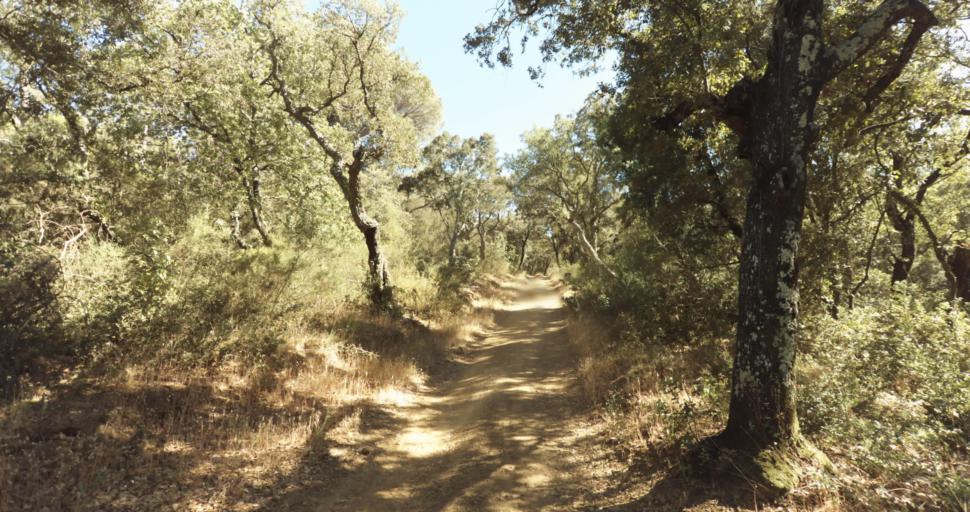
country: FR
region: Provence-Alpes-Cote d'Azur
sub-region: Departement du Var
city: Gassin
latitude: 43.2455
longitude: 6.5845
